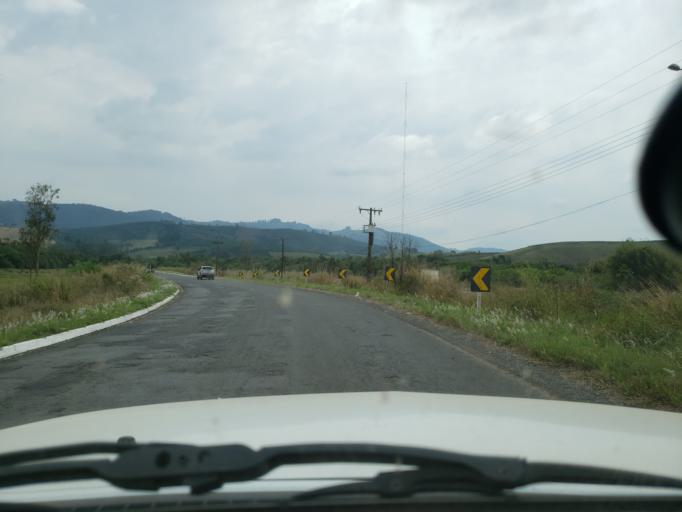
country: BR
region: Minas Gerais
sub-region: Jacutinga
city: Jacutinga
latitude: -22.2744
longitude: -46.6036
